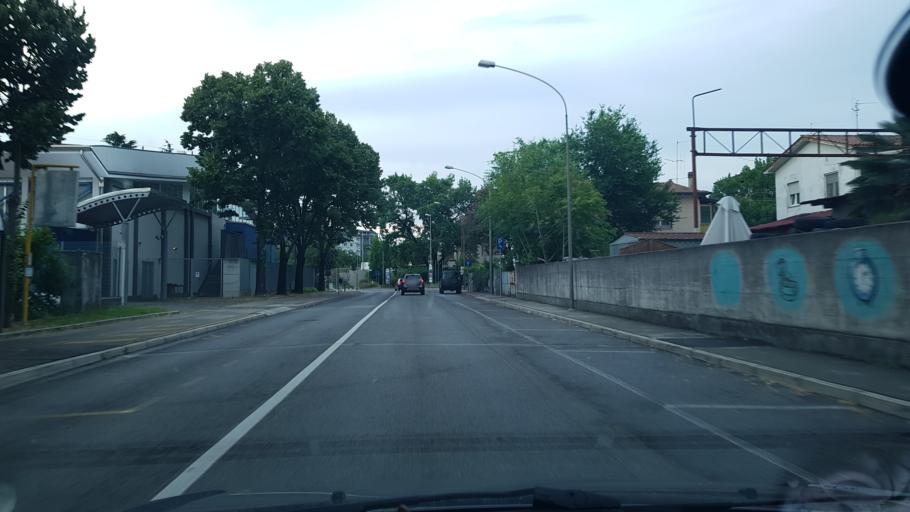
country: IT
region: Friuli Venezia Giulia
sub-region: Provincia di Gorizia
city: Gorizia
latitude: 45.9321
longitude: 13.6056
